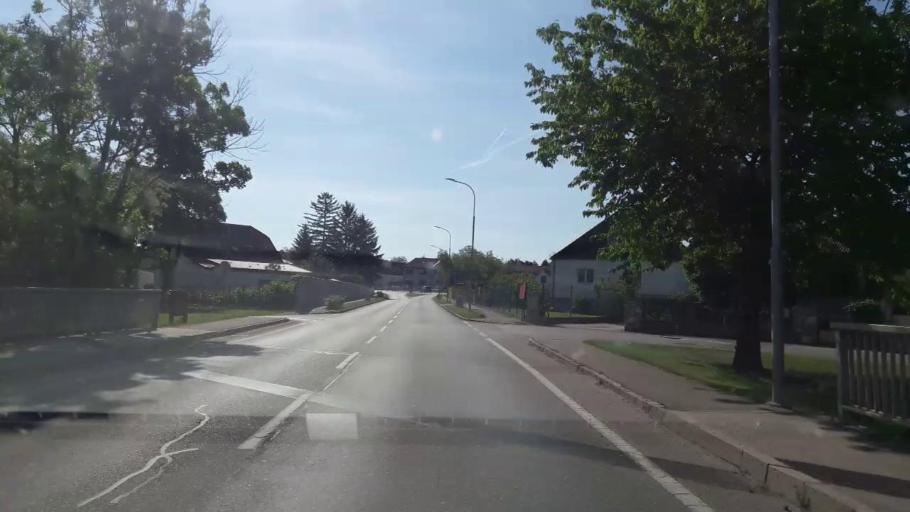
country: AT
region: Burgenland
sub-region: Eisenstadt-Umgebung
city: Trausdorf an der Wulka
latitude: 47.8140
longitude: 16.5506
